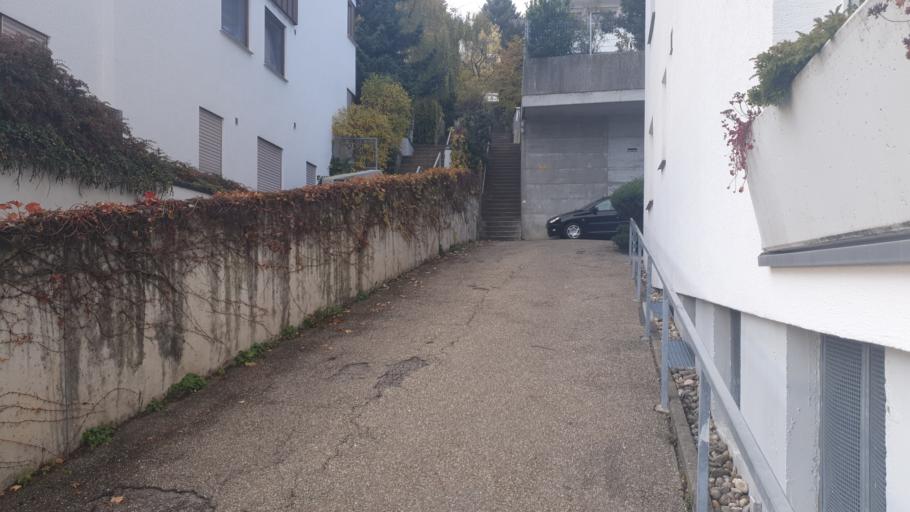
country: DE
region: Baden-Wuerttemberg
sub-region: Regierungsbezirk Stuttgart
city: Leonberg
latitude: 48.7907
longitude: 9.0294
